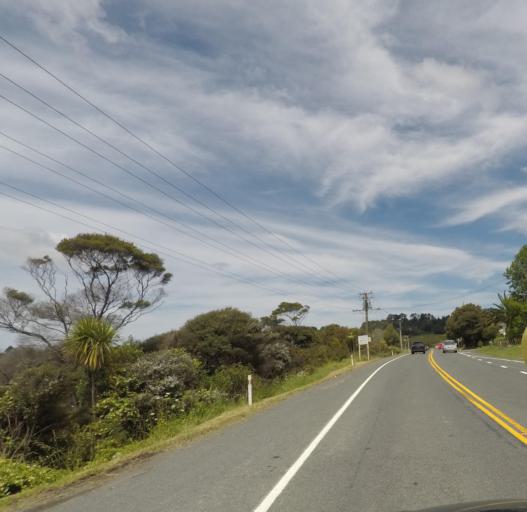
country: NZ
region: Auckland
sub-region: Auckland
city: Rothesay Bay
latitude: -36.6832
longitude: 174.7002
